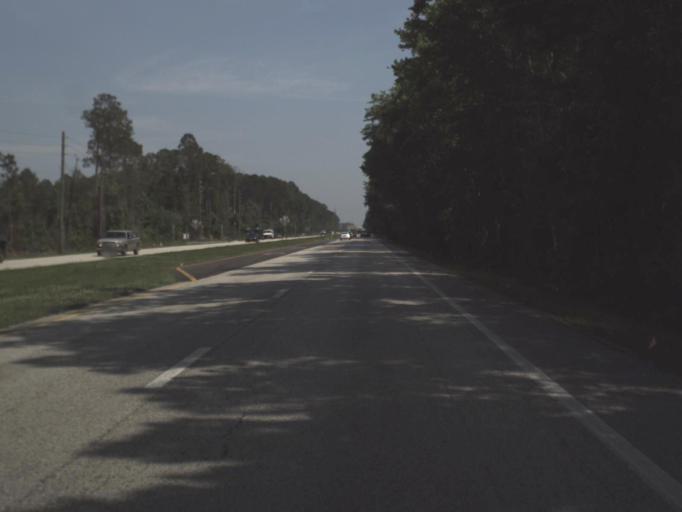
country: US
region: Florida
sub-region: Saint Johns County
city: Palm Valley
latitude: 30.1169
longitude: -81.4915
